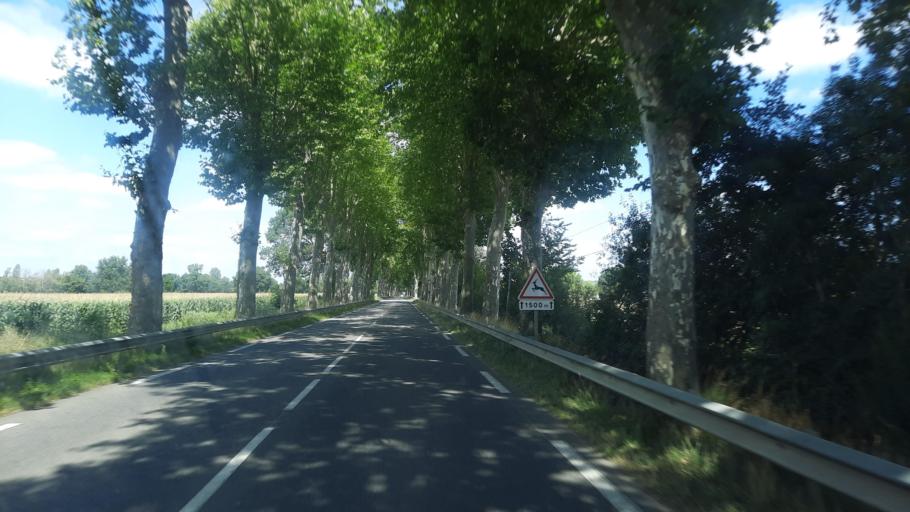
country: FR
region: Midi-Pyrenees
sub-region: Departement du Gers
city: Lombez
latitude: 43.4756
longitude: 0.9200
